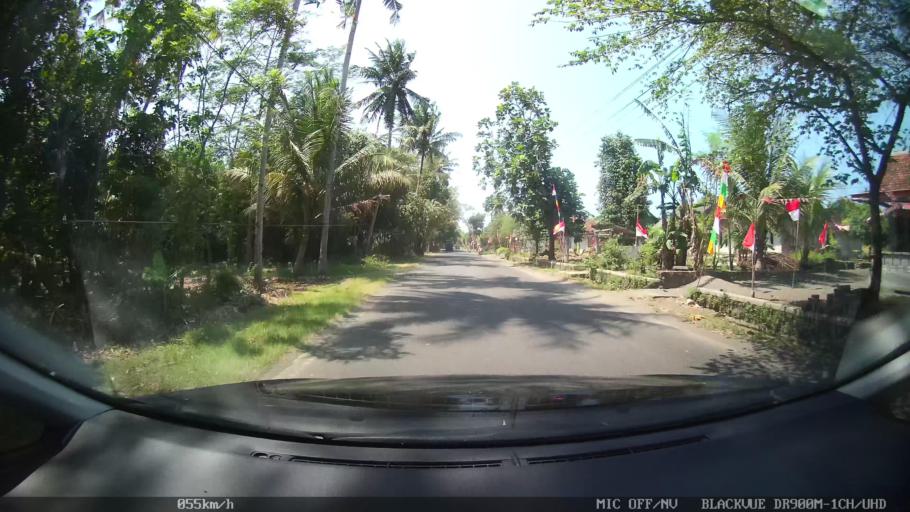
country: ID
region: Daerah Istimewa Yogyakarta
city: Srandakan
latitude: -7.9211
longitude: 110.1135
